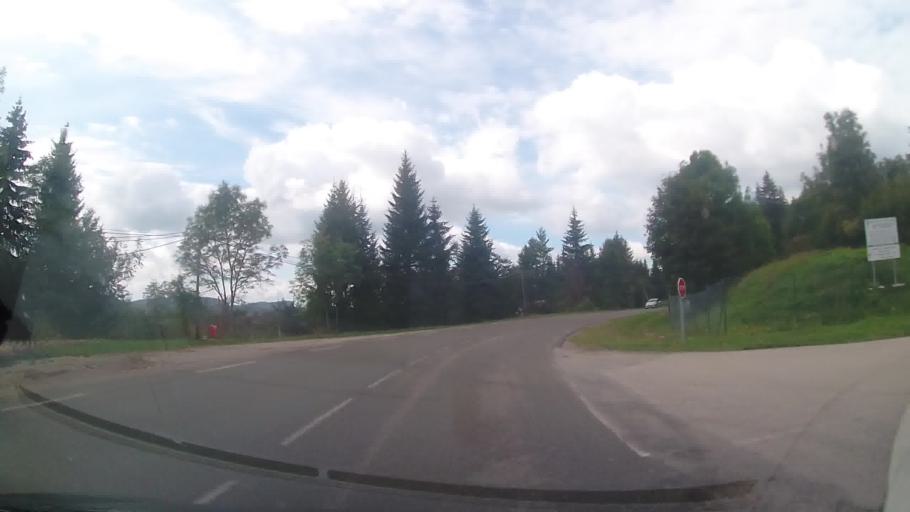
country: FR
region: Franche-Comte
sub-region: Departement du Jura
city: Les Rousses
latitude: 46.4589
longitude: 6.0740
